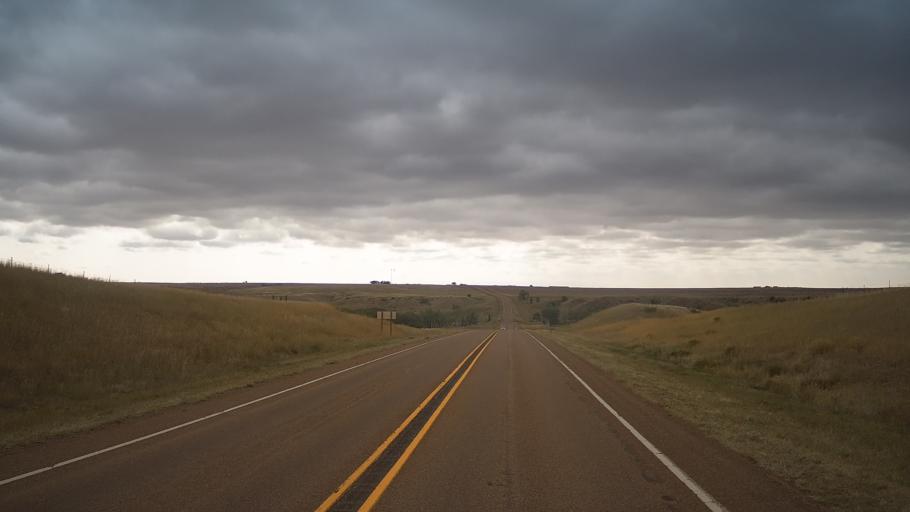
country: US
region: Montana
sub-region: Valley County
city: Glasgow
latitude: 48.3654
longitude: -106.7855
